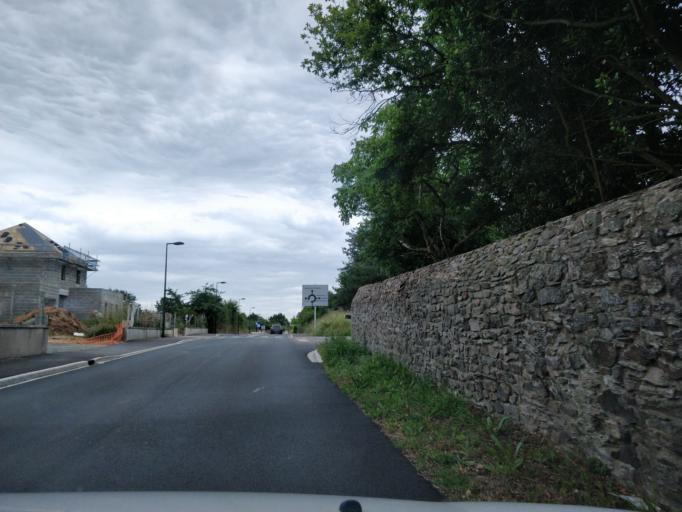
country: FR
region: Pays de la Loire
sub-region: Departement de Maine-et-Loire
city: Feneu
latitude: 47.5680
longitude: -0.5885
